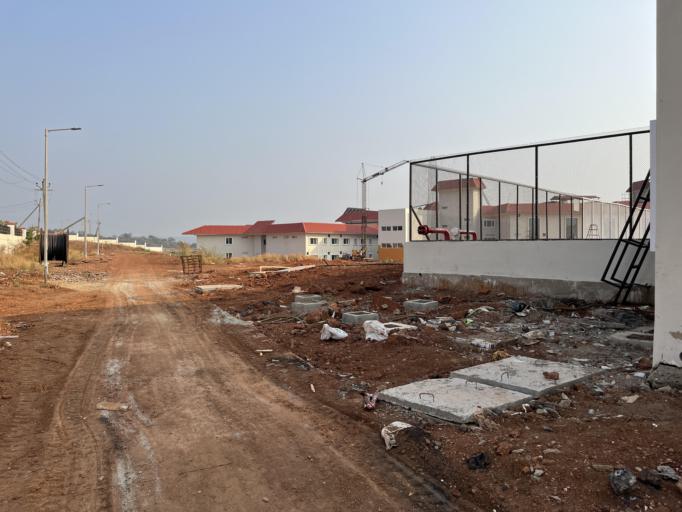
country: IN
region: Goa
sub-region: North Goa
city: Pernem
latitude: 15.6888
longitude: 73.8358
